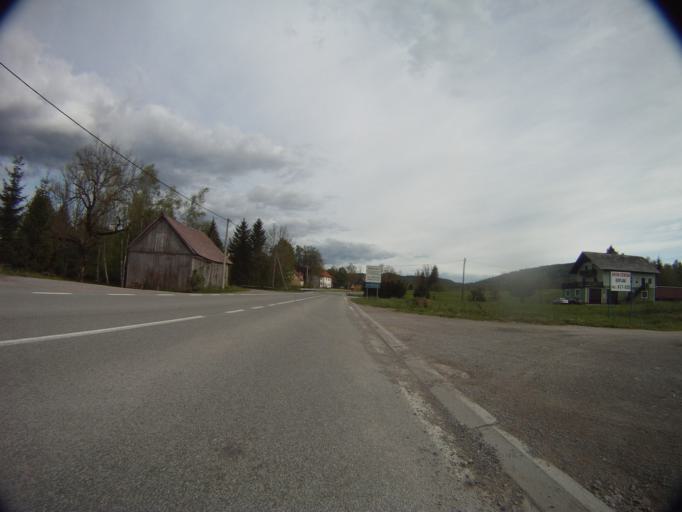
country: HR
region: Primorsko-Goranska
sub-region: Grad Delnice
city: Delnice
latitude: 45.3894
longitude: 14.8849
